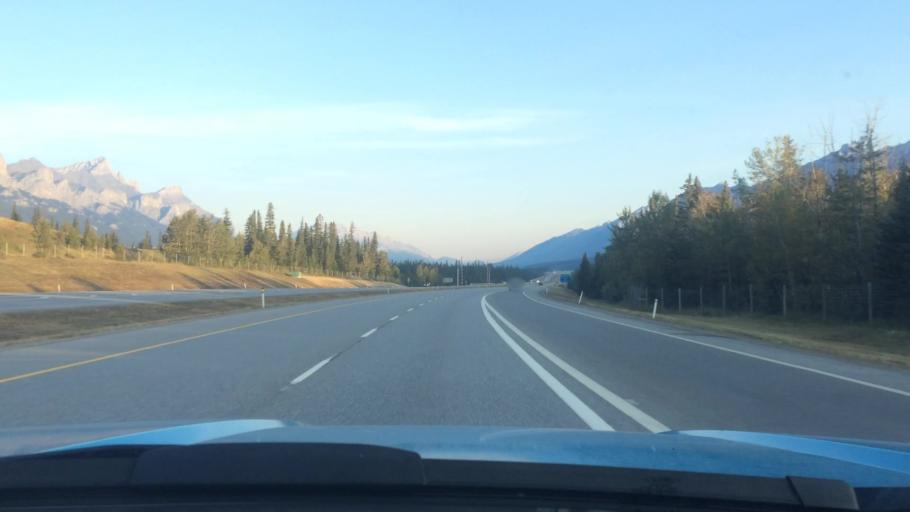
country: CA
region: Alberta
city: Canmore
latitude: 51.0589
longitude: -115.3192
